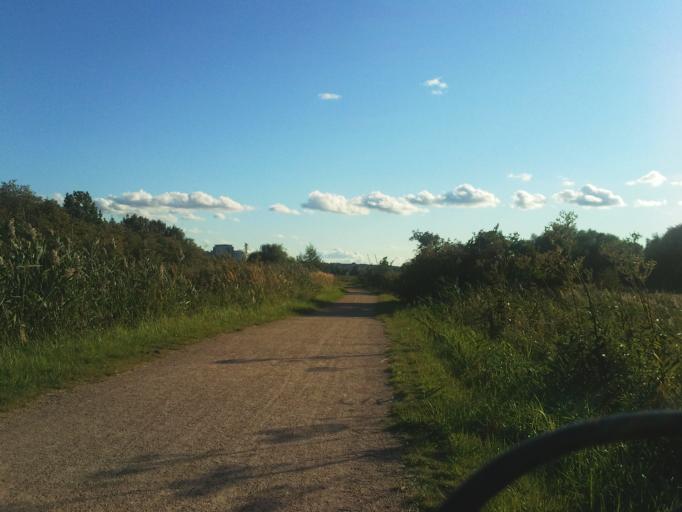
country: DE
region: Mecklenburg-Vorpommern
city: Dierkow-West
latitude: 54.1012
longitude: 12.1387
